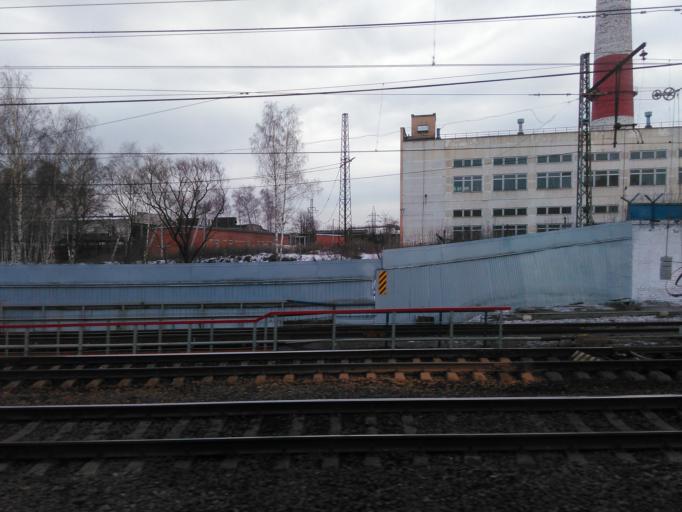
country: RU
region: Moskovskaya
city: Mytishchi
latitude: 55.9096
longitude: 37.7550
